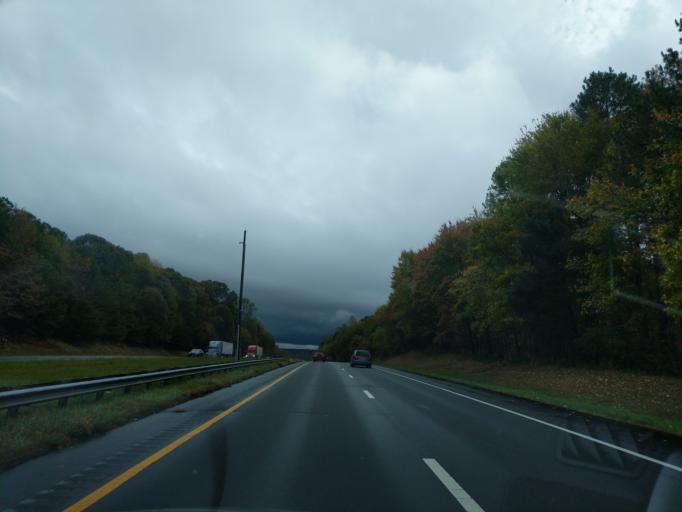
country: US
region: North Carolina
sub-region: Orange County
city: Hillsborough
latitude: 36.0469
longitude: -79.0481
